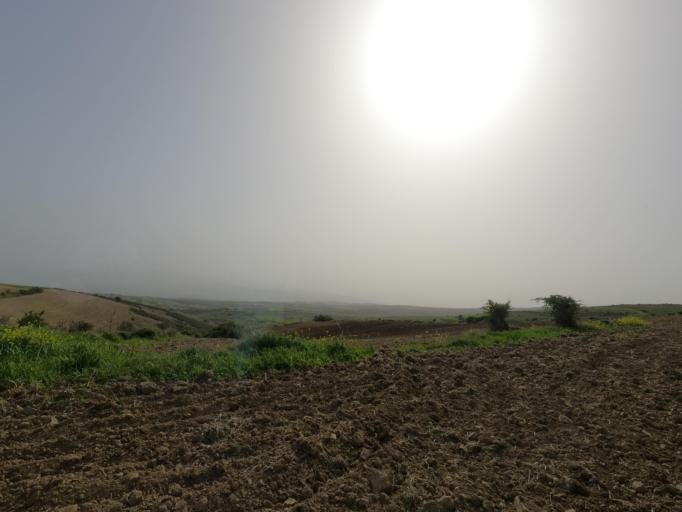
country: CY
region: Pafos
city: Polis
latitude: 35.0047
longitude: 32.3498
